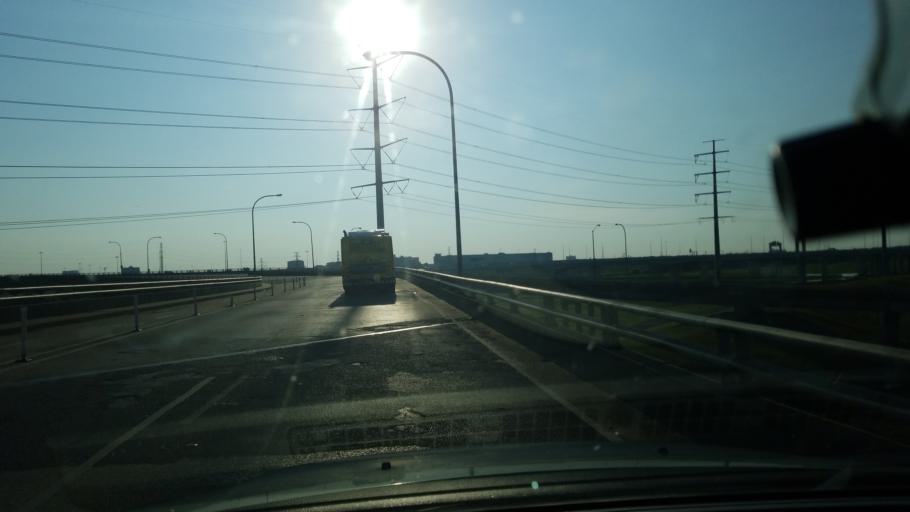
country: US
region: Texas
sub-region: Dallas County
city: Dallas
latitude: 32.7627
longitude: -96.8136
